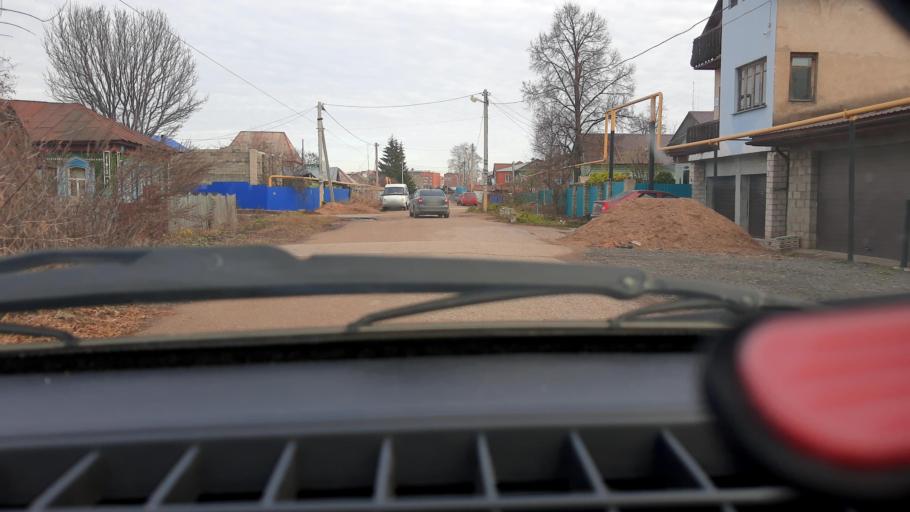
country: RU
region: Bashkortostan
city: Ufa
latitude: 54.7782
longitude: 56.0598
